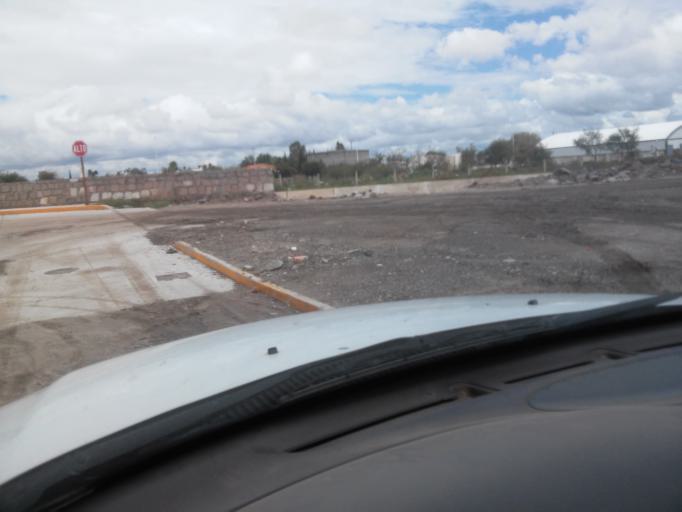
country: MX
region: Durango
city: Victoria de Durango
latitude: 24.0251
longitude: -104.6158
